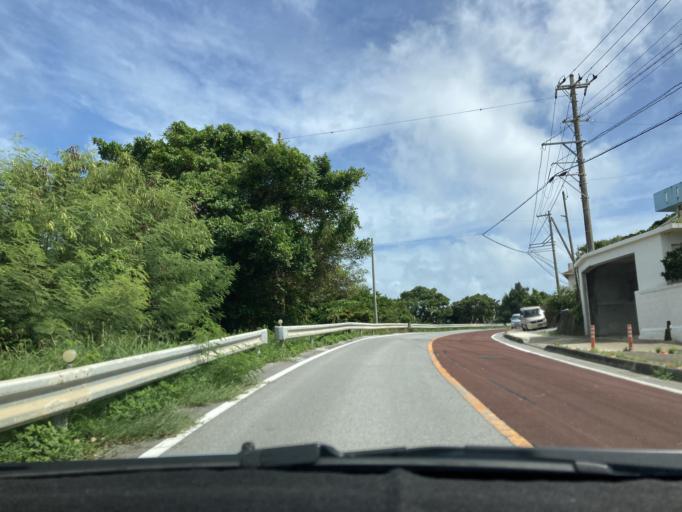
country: JP
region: Okinawa
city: Ginowan
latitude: 26.1782
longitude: 127.8254
